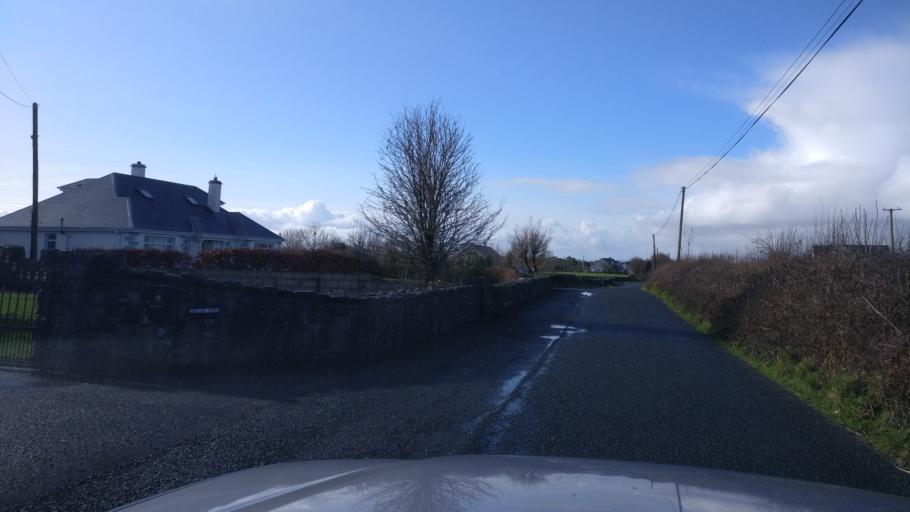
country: IE
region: Connaught
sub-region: County Galway
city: Athenry
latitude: 53.2429
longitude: -8.7722
